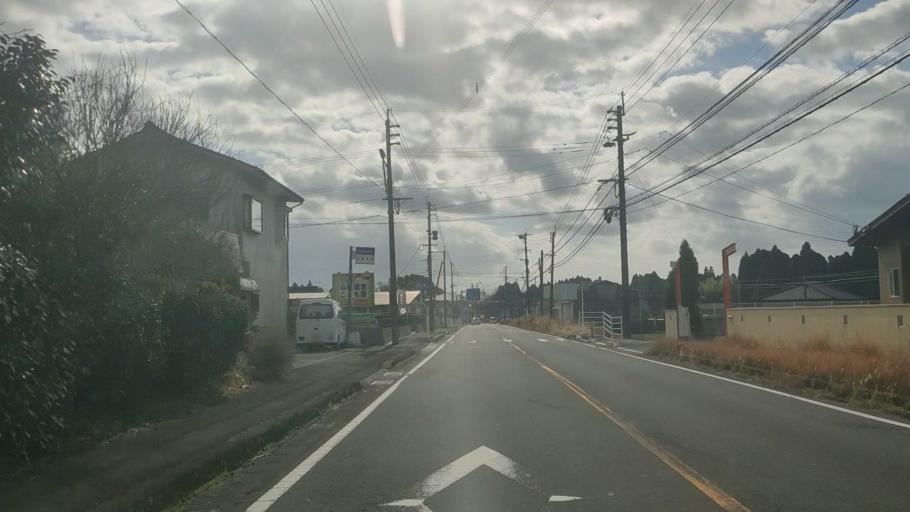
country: JP
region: Kagoshima
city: Kajiki
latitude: 31.7800
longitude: 130.7037
